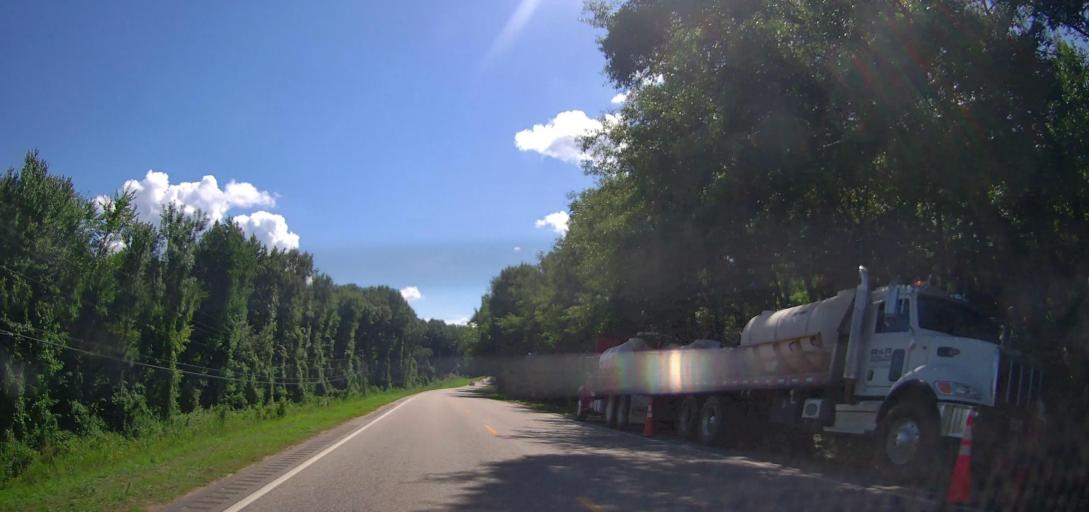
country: US
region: Alabama
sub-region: Macon County
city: Tuskegee
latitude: 32.3785
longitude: -85.8304
